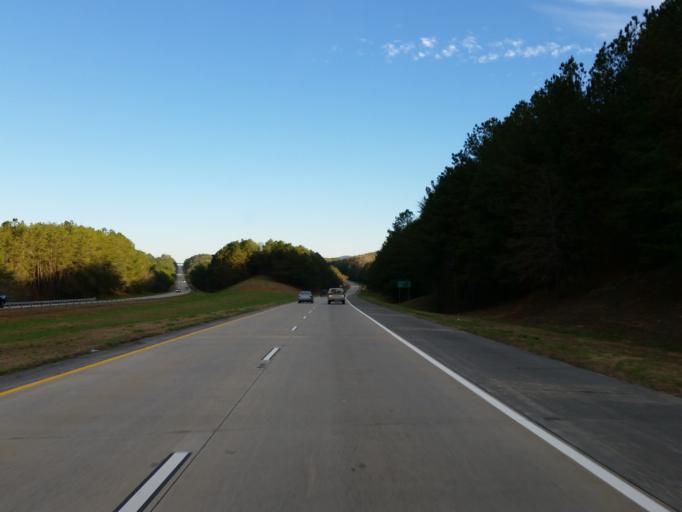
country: US
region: Georgia
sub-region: Cherokee County
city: Ball Ground
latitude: 34.3390
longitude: -84.3917
